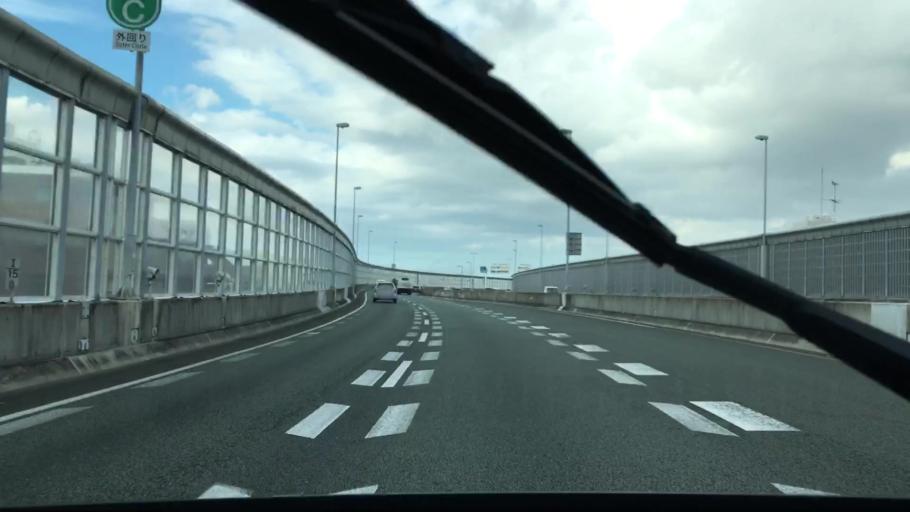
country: JP
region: Fukuoka
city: Fukuoka-shi
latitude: 33.5852
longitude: 130.3405
